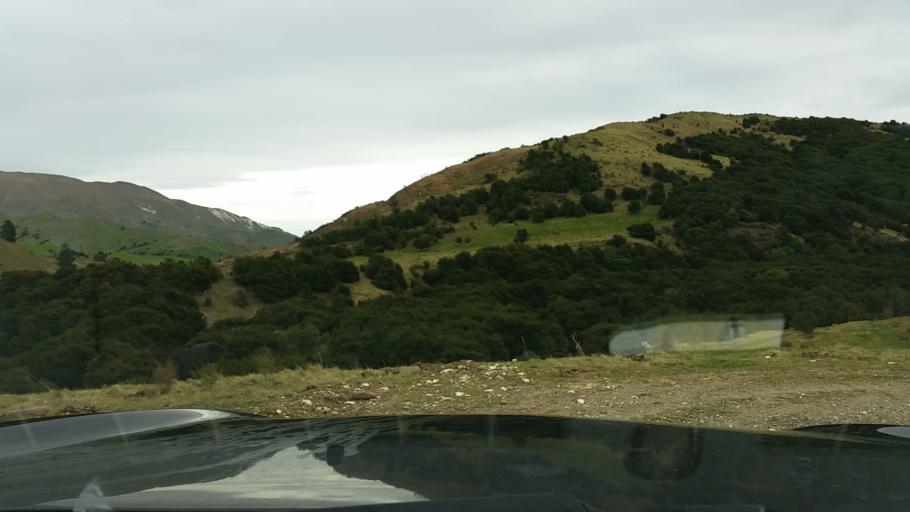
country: NZ
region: Marlborough
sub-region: Marlborough District
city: Blenheim
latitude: -41.8829
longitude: 174.0754
